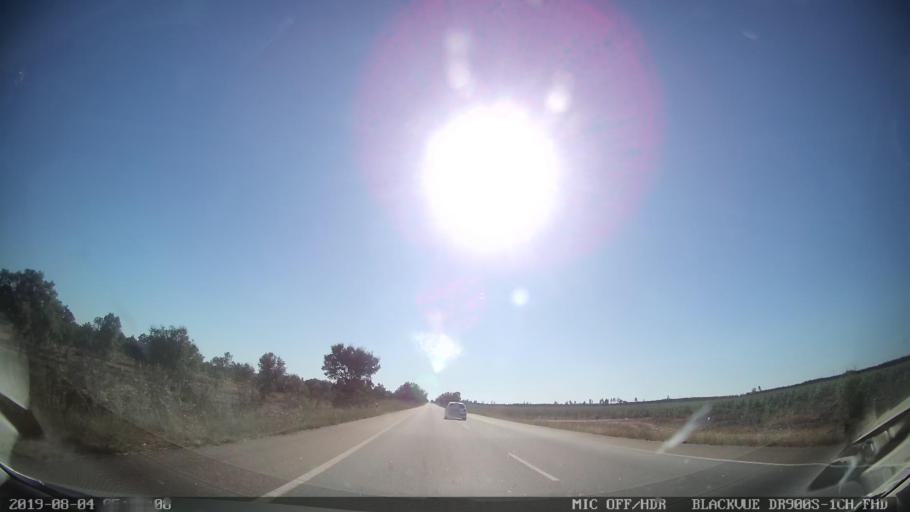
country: PT
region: Portalegre
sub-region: Gaviao
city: Gaviao
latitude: 39.4460
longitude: -7.8188
